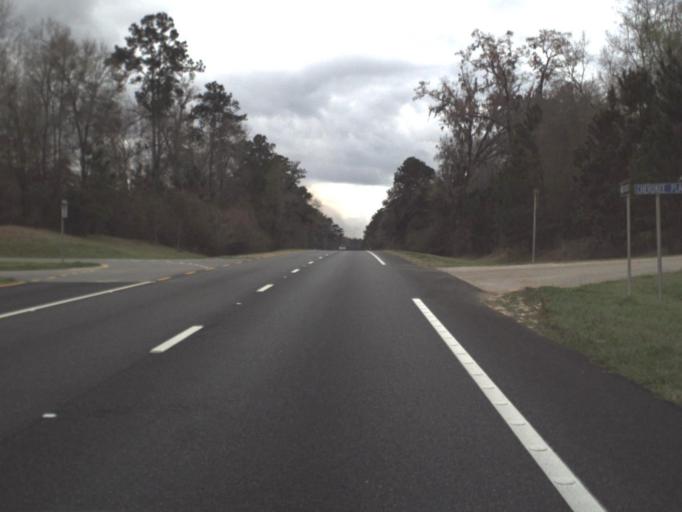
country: US
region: Florida
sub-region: Leon County
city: Tallahassee
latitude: 30.6348
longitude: -84.1694
